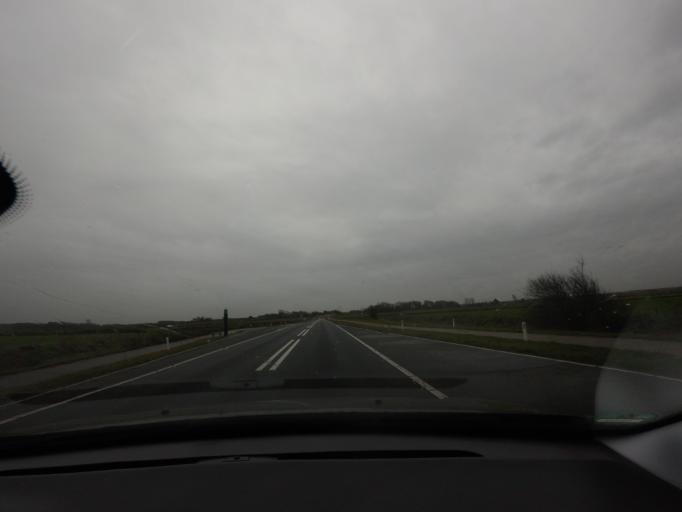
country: NL
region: North Holland
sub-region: Gemeente Texel
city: Den Burg
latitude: 53.0418
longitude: 4.8001
